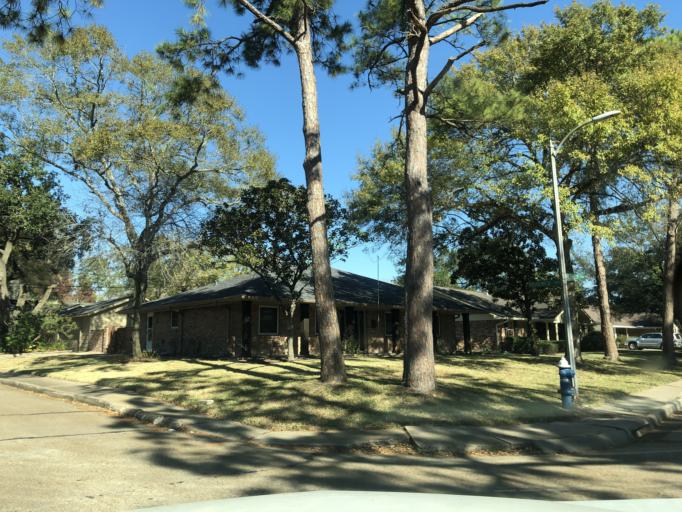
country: US
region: Texas
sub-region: Harris County
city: Bellaire
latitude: 29.6802
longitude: -95.4977
